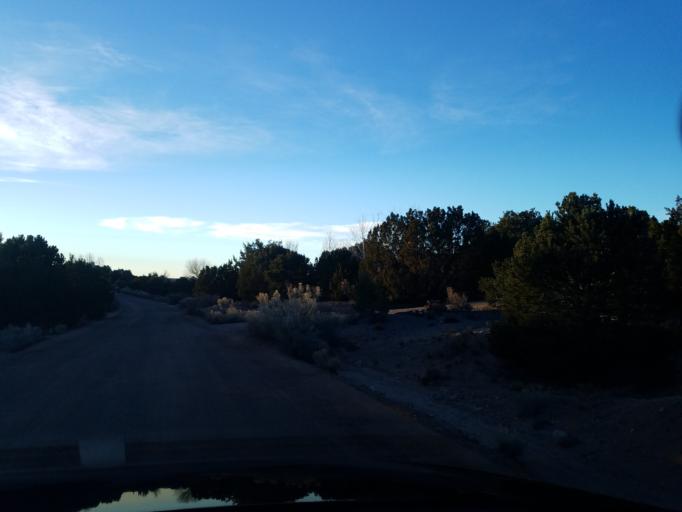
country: US
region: New Mexico
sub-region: Santa Fe County
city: Agua Fria
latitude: 35.6747
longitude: -105.9994
